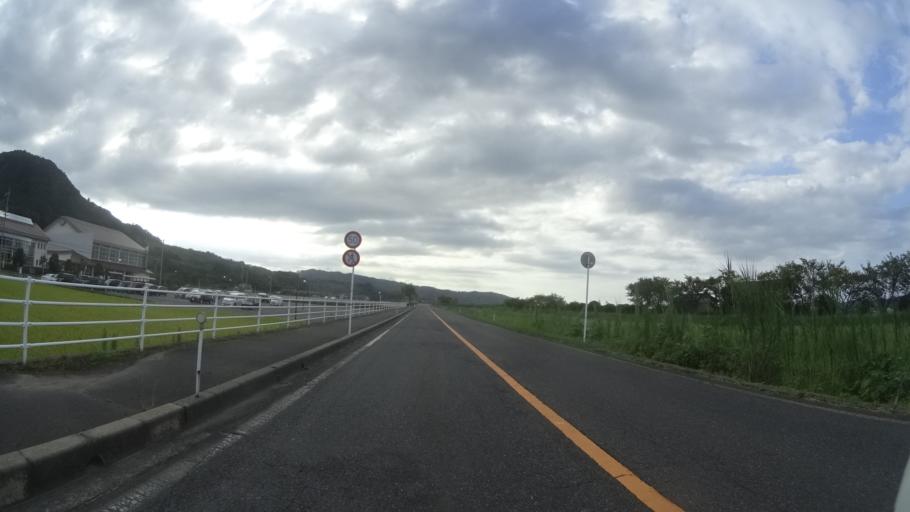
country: JP
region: Tottori
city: Kurayoshi
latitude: 35.4630
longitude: 133.9031
